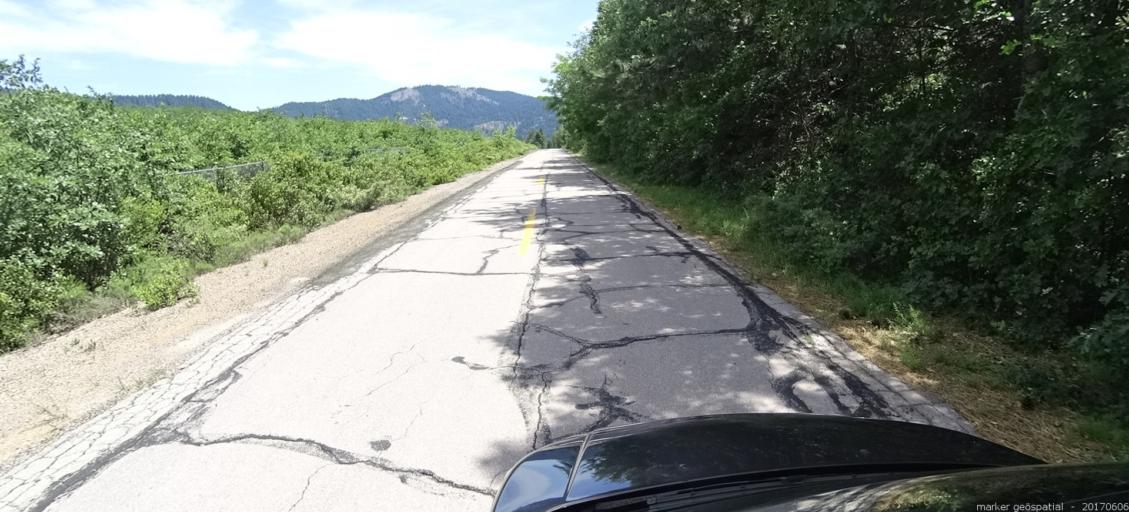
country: US
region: California
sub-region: Siskiyou County
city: Dunsmuir
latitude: 41.2625
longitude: -122.2728
